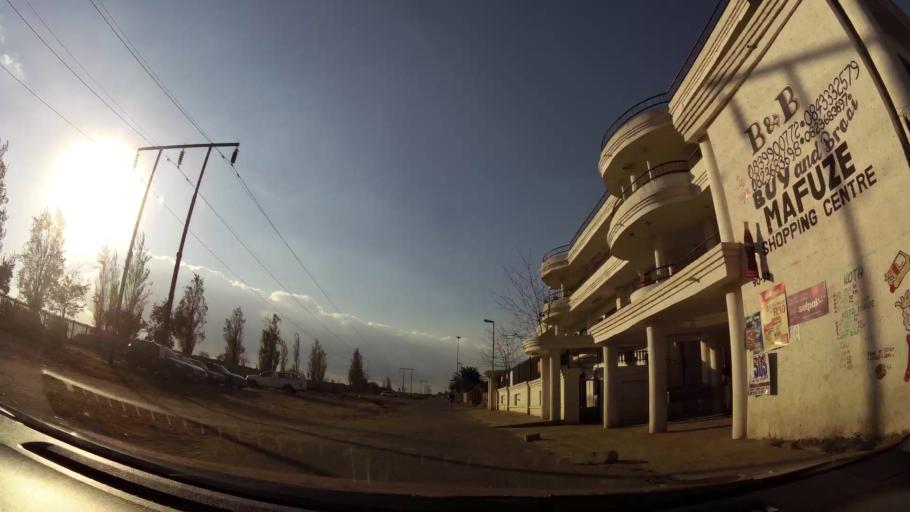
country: ZA
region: Gauteng
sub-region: City of Johannesburg Metropolitan Municipality
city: Soweto
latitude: -26.2359
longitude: 27.8589
